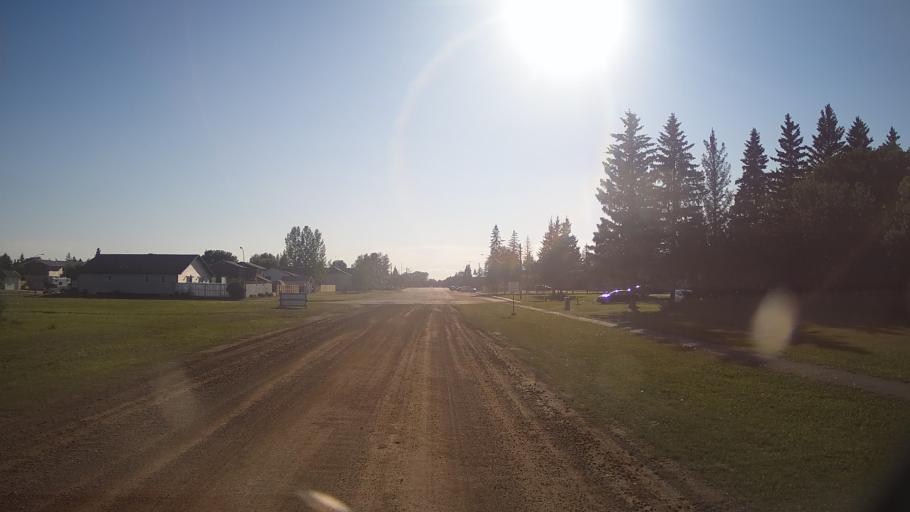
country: CA
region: Saskatchewan
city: Lanigan
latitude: 51.8508
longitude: -105.0222
